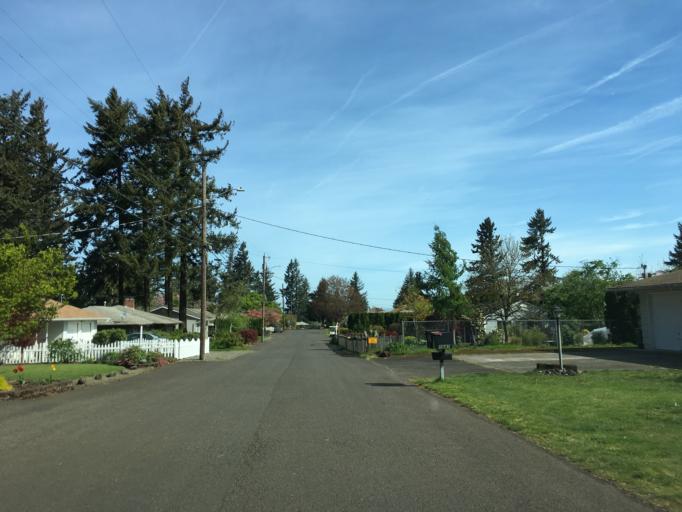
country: US
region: Oregon
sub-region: Multnomah County
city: Lents
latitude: 45.5349
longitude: -122.5168
